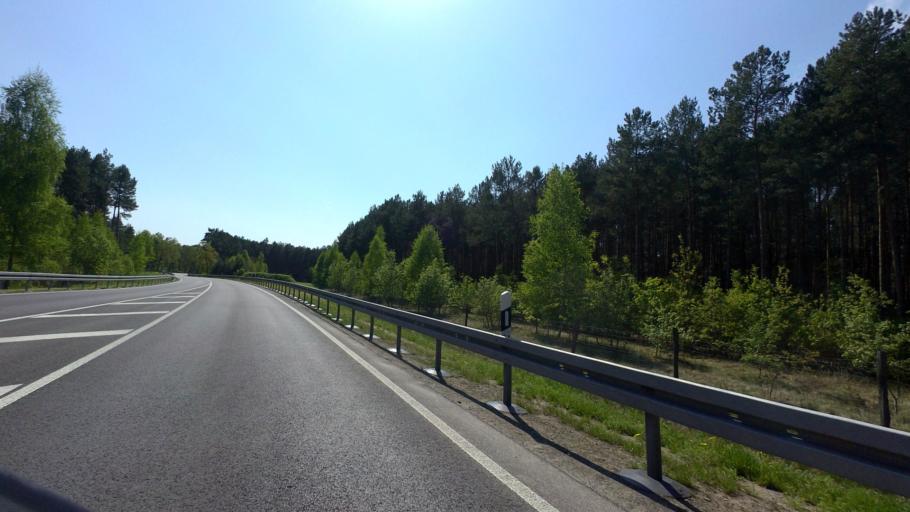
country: DE
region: Brandenburg
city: Beeskow
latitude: 52.1508
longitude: 14.2145
